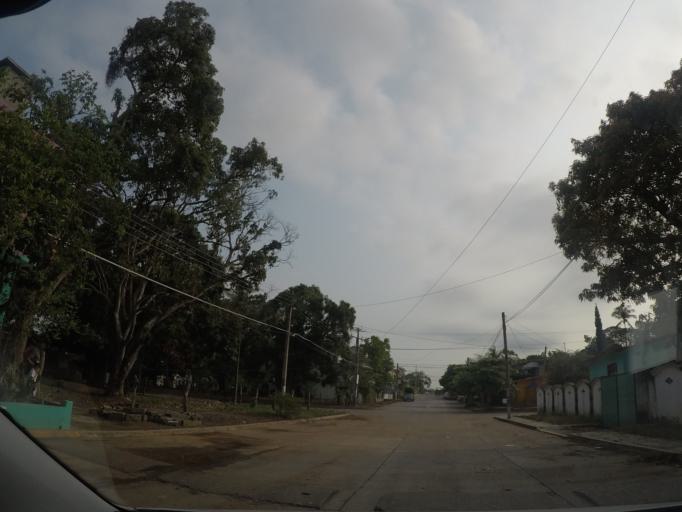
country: MX
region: Oaxaca
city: Colonia Rincon Viejo
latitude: 16.8847
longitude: -95.0441
